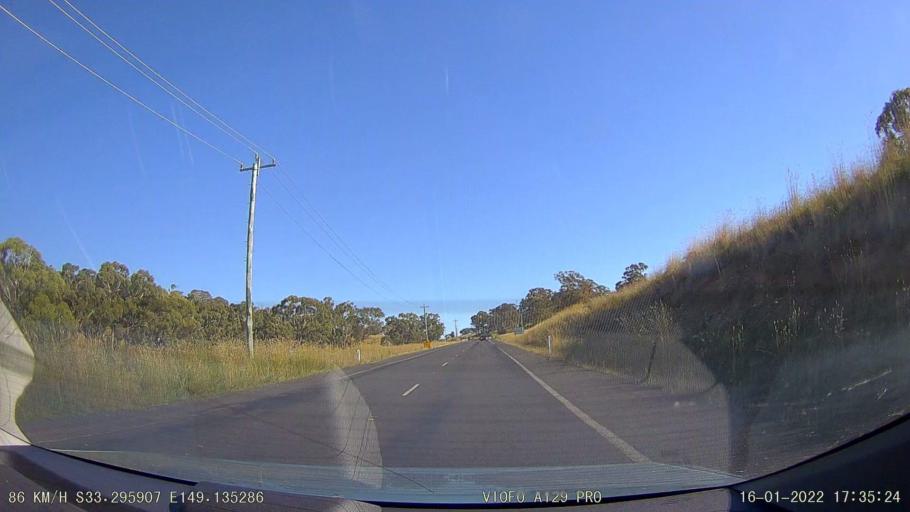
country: AU
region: New South Wales
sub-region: Orange Municipality
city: Orange
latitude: -33.2957
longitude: 149.1353
